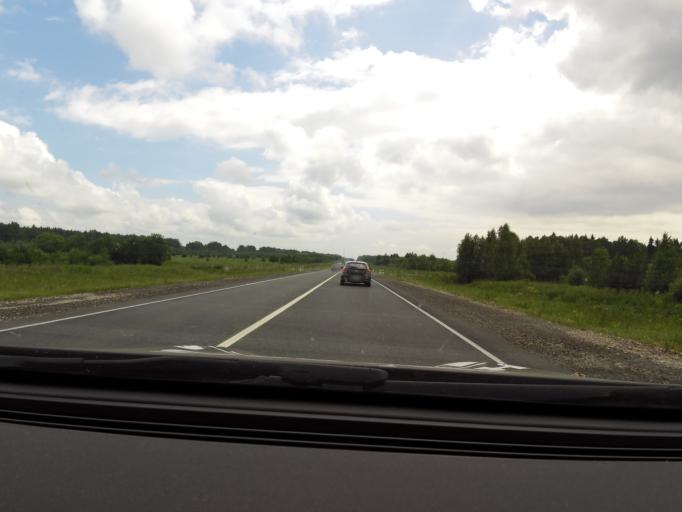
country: RU
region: Perm
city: Orda
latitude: 57.2202
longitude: 57.0829
